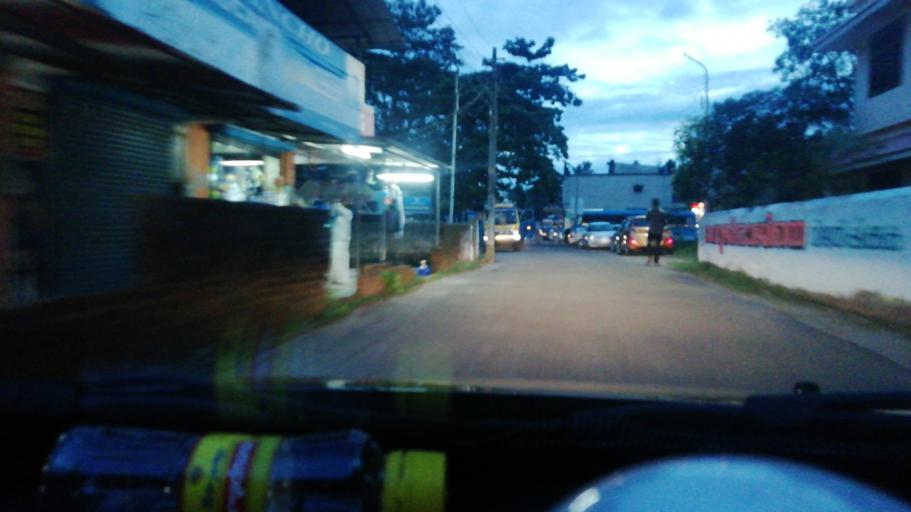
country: IN
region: Kerala
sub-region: Thiruvananthapuram
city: Paravur
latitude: 8.8118
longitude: 76.6687
